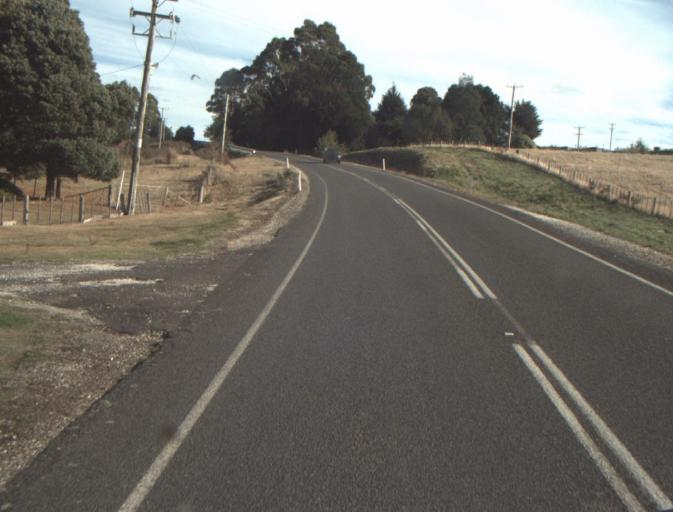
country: AU
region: Tasmania
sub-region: Launceston
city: Mayfield
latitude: -41.2820
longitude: 147.2191
